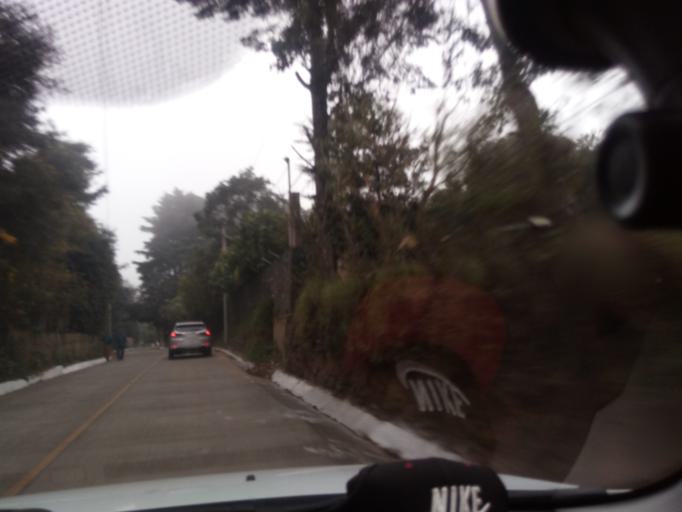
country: GT
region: Sacatepequez
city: San Bartolome Milpas Altas
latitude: 14.5924
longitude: -90.7058
